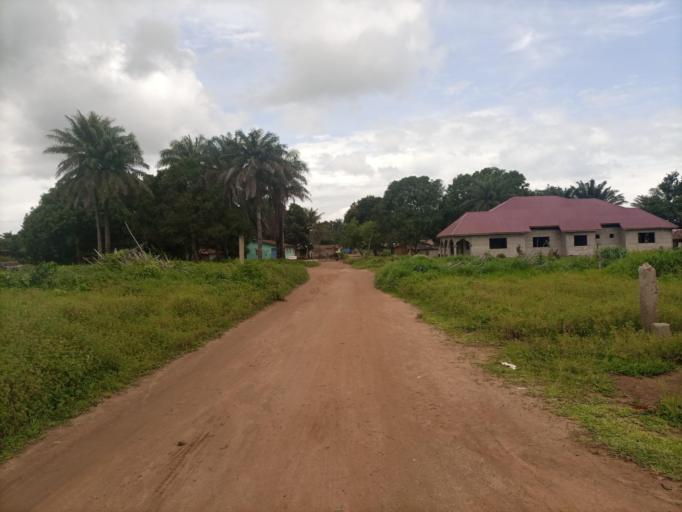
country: SL
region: Northern Province
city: Masoyila
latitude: 8.5918
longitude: -13.1645
